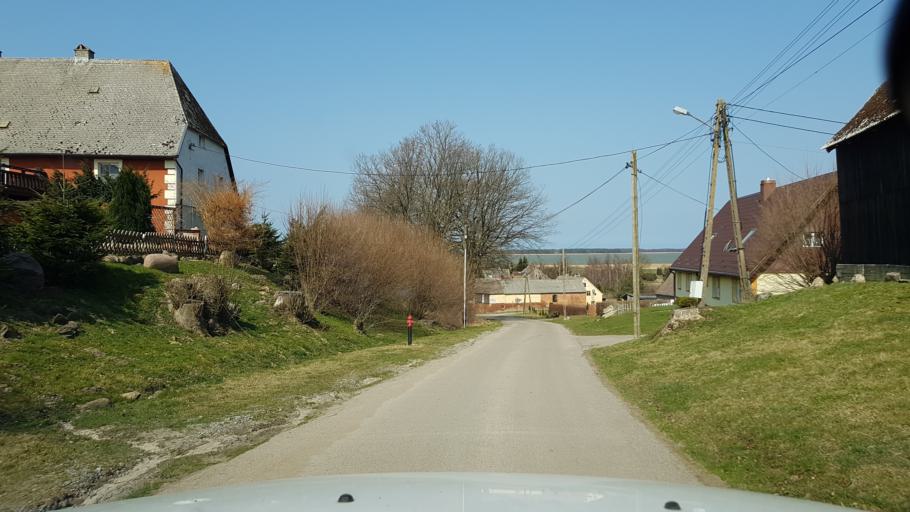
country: PL
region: West Pomeranian Voivodeship
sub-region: Powiat slawienski
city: Darlowo
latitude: 54.4588
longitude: 16.4340
